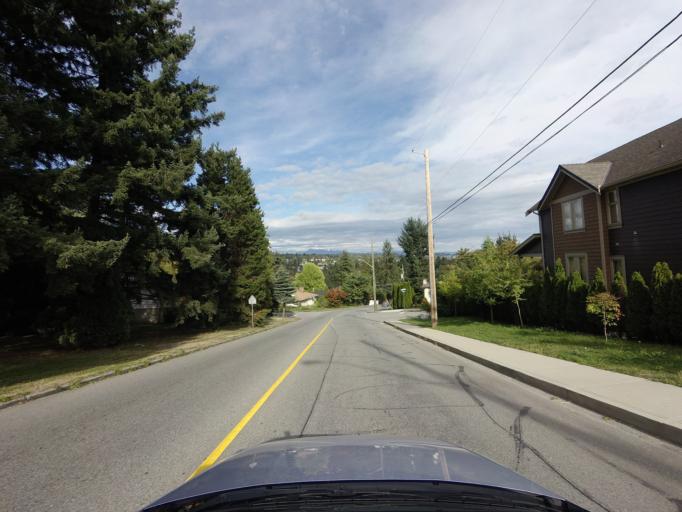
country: CA
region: British Columbia
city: New Westminster
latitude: 49.2356
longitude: -122.8962
